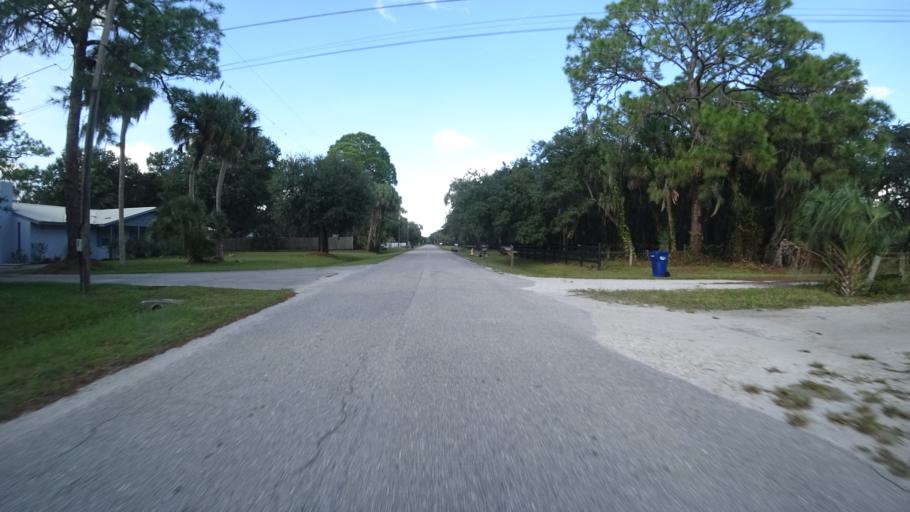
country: US
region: Florida
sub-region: Manatee County
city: Ellenton
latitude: 27.4846
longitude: -82.4754
